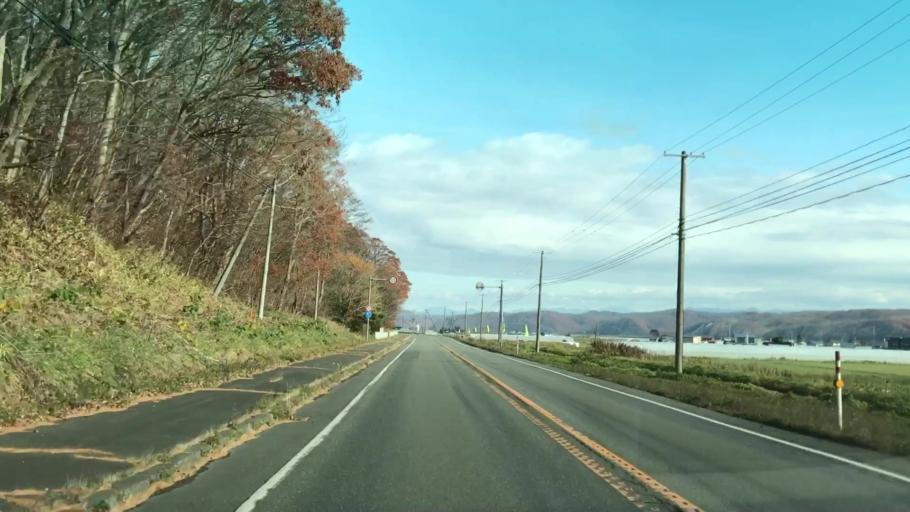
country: JP
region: Hokkaido
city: Shizunai-furukawacho
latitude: 42.5615
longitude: 142.0855
